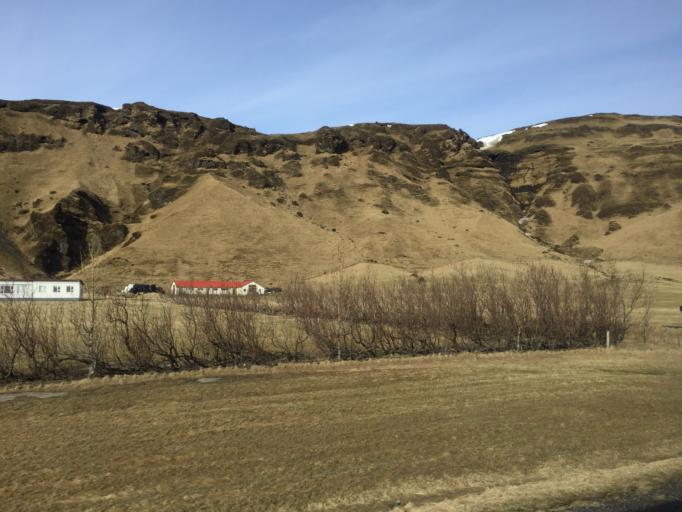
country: IS
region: South
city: Vestmannaeyjar
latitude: 63.4546
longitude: -19.0806
